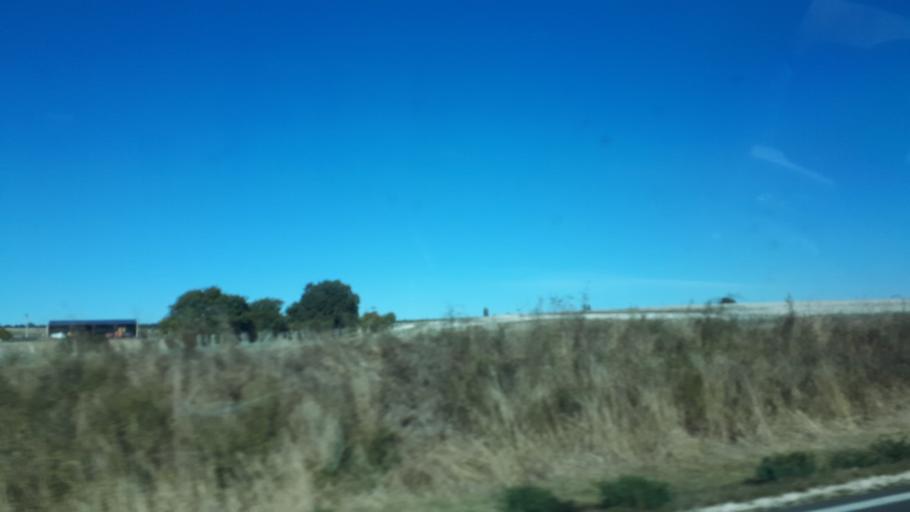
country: FR
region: Centre
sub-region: Departement du Loir-et-Cher
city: Moree
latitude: 47.9412
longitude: 1.2065
